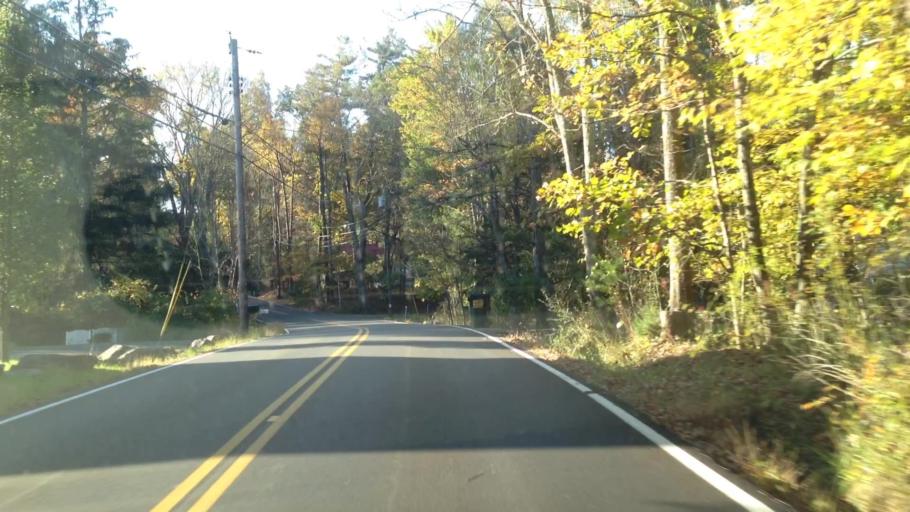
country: US
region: New York
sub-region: Ulster County
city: Tillson
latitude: 41.8306
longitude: -74.0402
